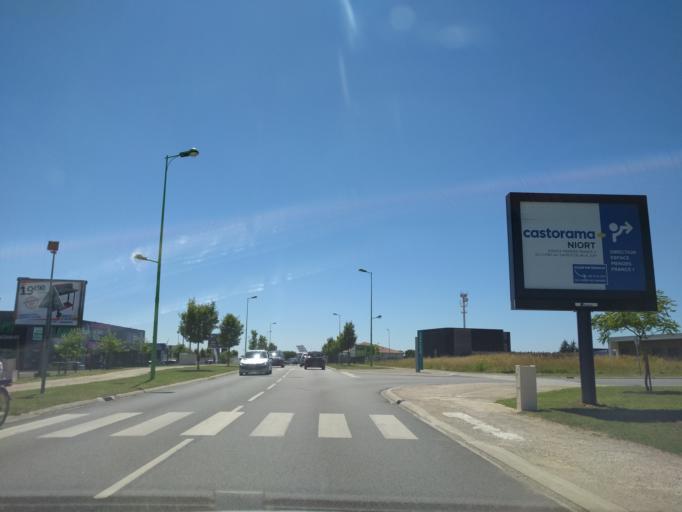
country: FR
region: Poitou-Charentes
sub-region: Departement des Deux-Sevres
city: Chauray
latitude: 46.3374
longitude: -0.3987
